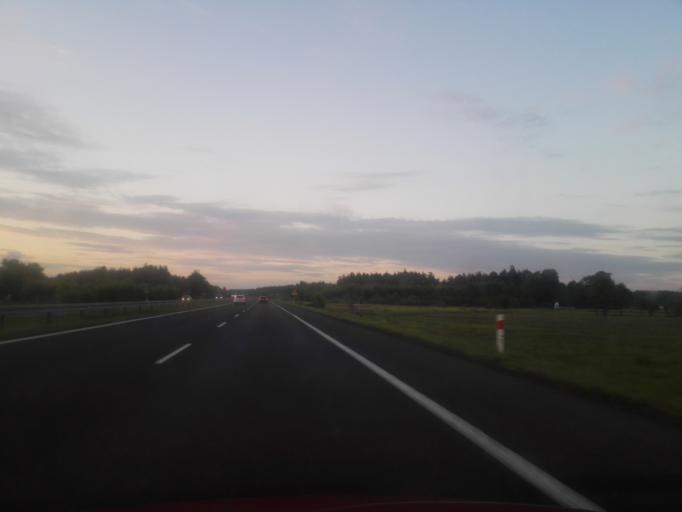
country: PL
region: Lodz Voivodeship
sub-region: Powiat radomszczanski
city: Radomsko
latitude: 51.0520
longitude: 19.3552
